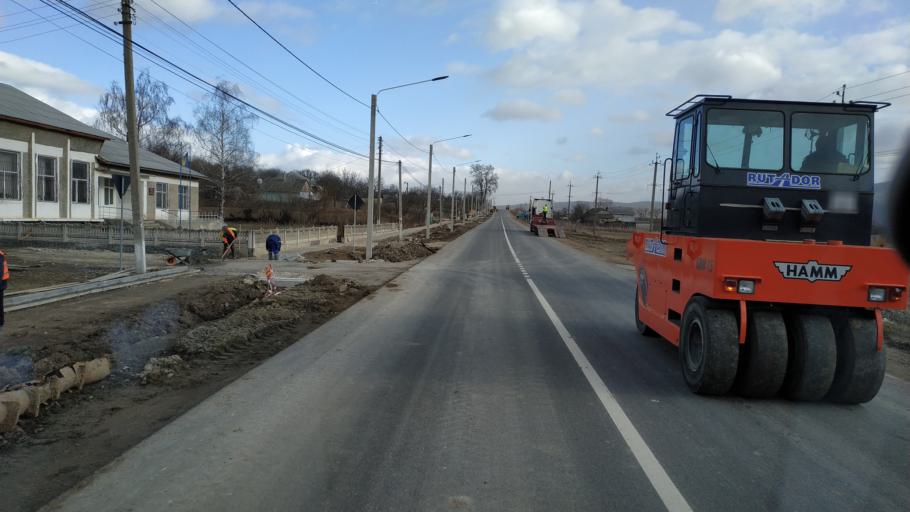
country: MD
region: Calarasi
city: Calarasi
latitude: 47.3196
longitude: 28.1107
